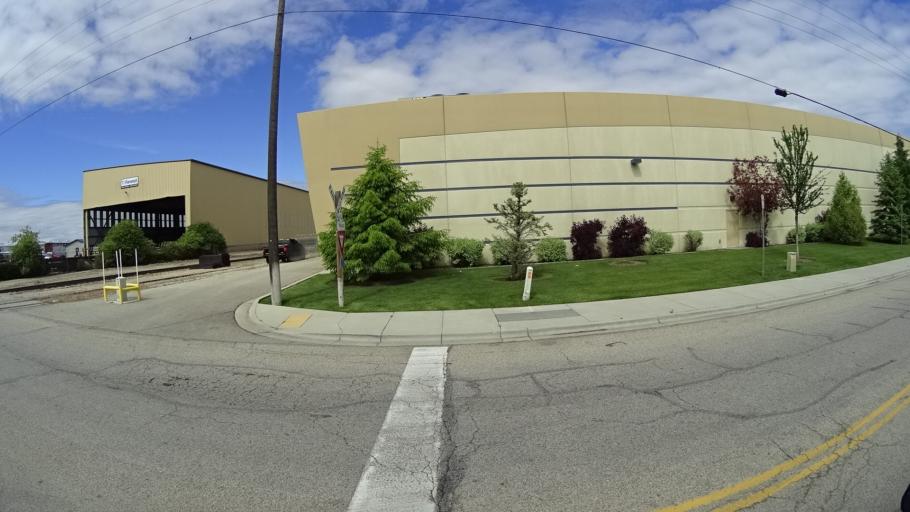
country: US
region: Idaho
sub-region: Ada County
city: Boise
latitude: 43.5628
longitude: -116.1986
